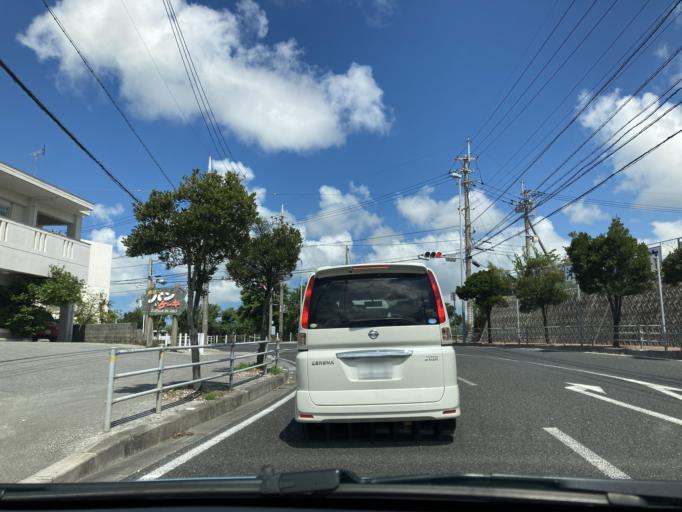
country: JP
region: Okinawa
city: Tomigusuku
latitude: 26.1715
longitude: 127.7221
